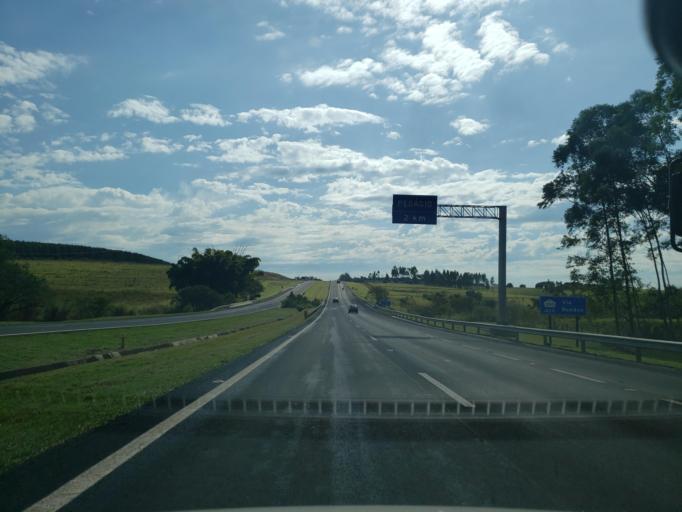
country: BR
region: Sao Paulo
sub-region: Pirajui
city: Pirajui
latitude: -21.9742
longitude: -49.4535
